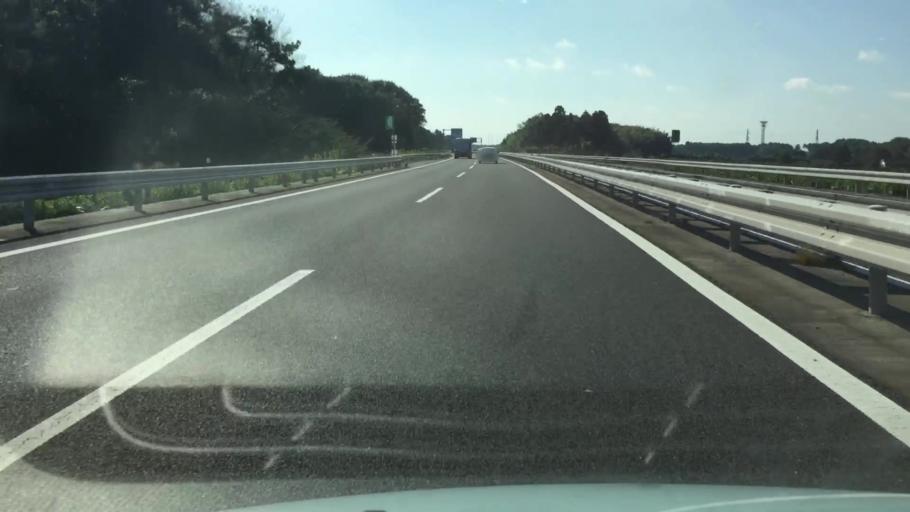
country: JP
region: Tochigi
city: Mooka
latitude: 36.4987
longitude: 139.9896
